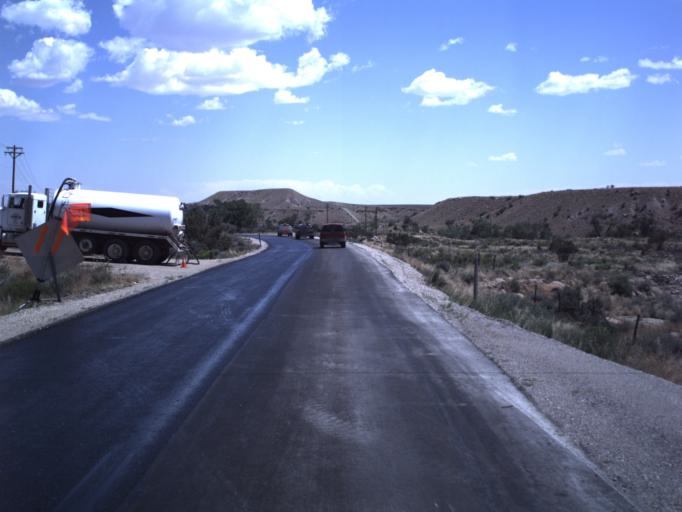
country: US
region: Utah
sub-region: Emery County
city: Orangeville
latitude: 39.2522
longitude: -111.0939
